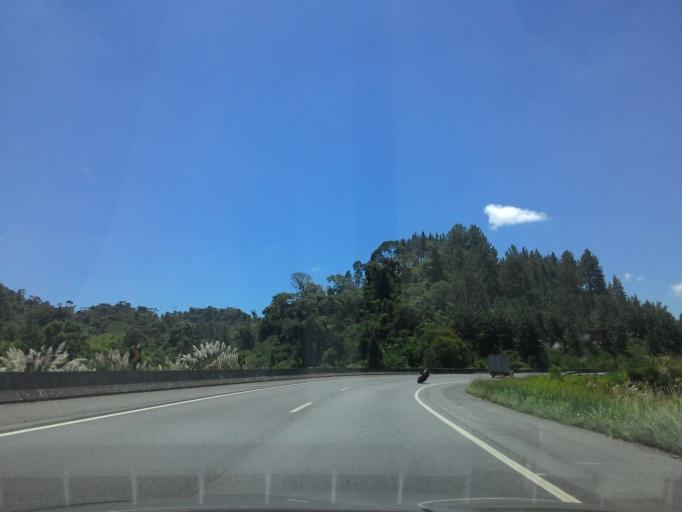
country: BR
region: Parana
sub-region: Antonina
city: Antonina
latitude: -25.0565
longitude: -48.5550
